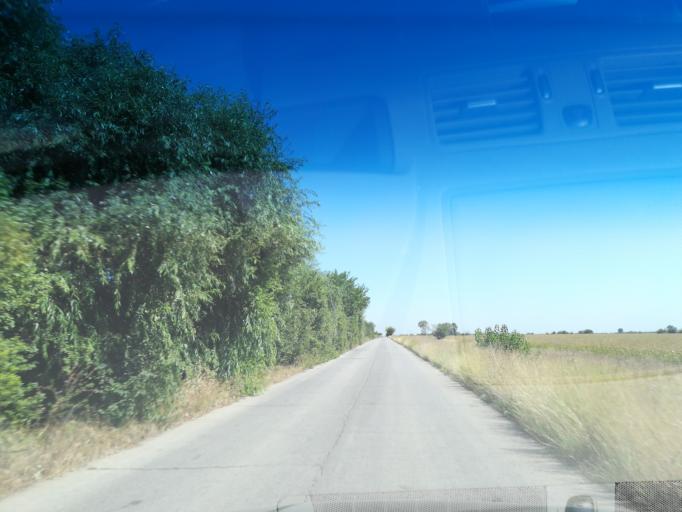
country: BG
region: Plovdiv
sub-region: Obshtina Suedinenie
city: Suedinenie
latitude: 42.2513
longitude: 24.4722
